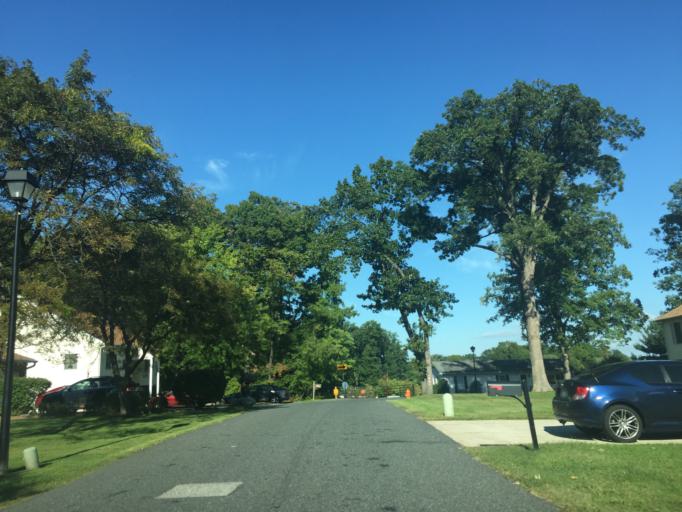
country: US
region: Maryland
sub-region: Baltimore County
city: Rossville
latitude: 39.3503
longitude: -76.4726
